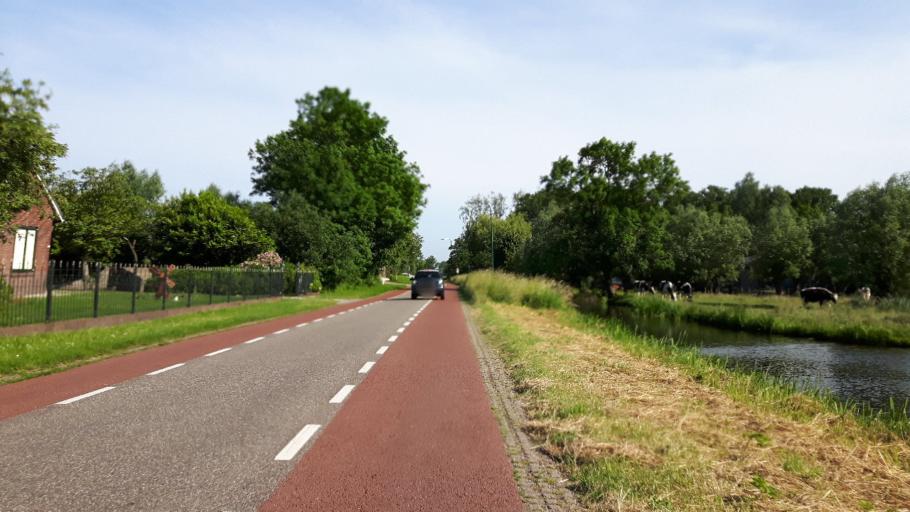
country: NL
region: Utrecht
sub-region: Stichtse Vecht
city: Breukelen
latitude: 52.1727
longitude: 4.9447
